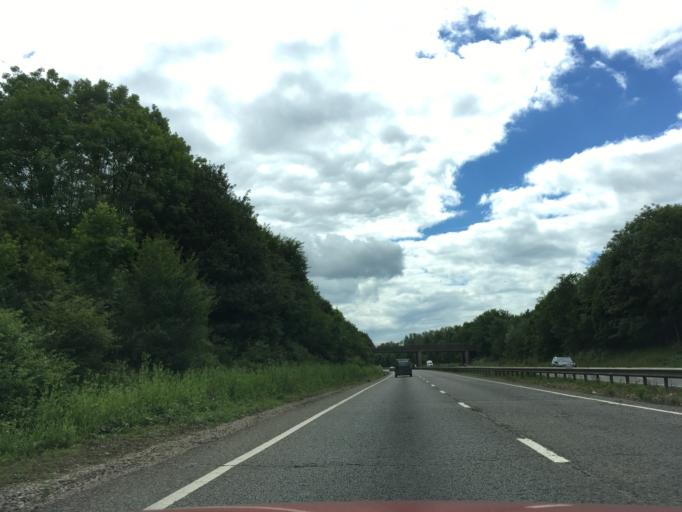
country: GB
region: England
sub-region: Milton Keynes
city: Milton Keynes
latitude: 52.0196
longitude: -0.7584
